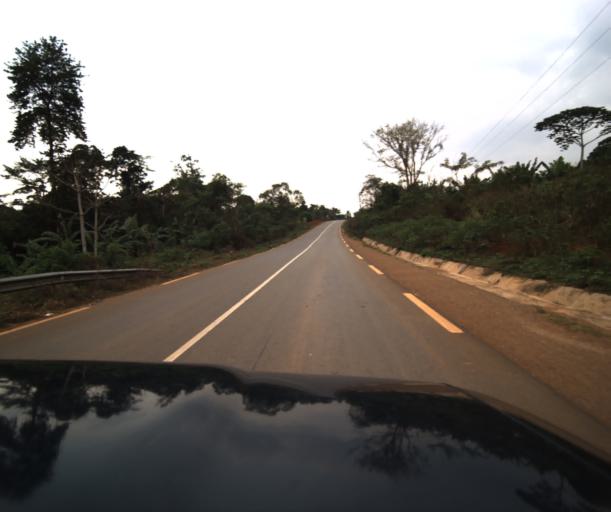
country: CM
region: Centre
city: Mbankomo
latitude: 3.7865
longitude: 11.4174
